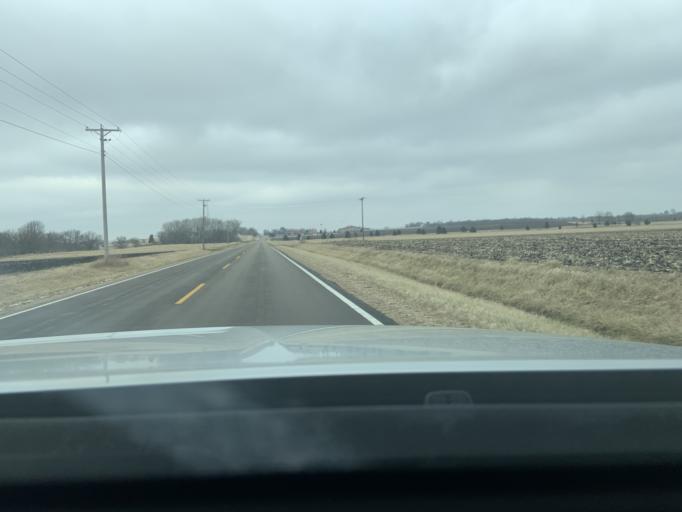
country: US
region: Illinois
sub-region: LaSalle County
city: Seneca
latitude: 41.3830
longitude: -88.6133
